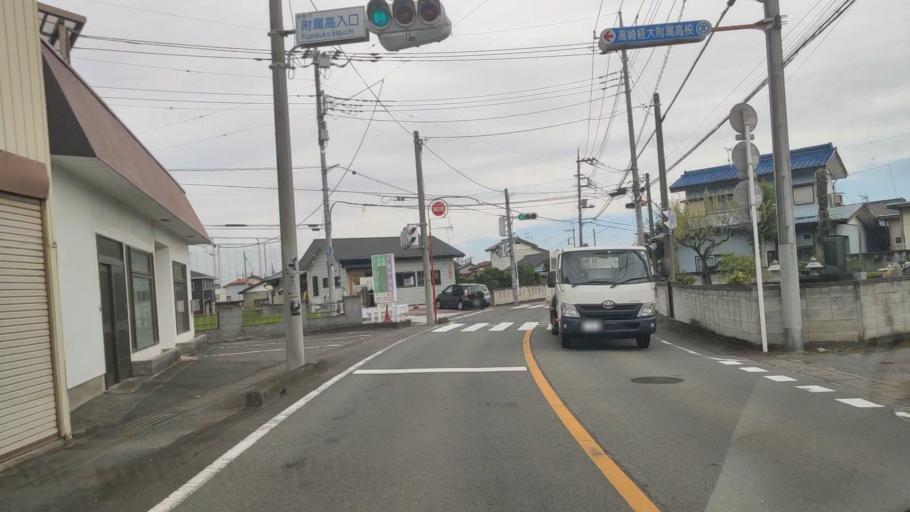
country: JP
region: Gunma
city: Takasaki
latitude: 36.3593
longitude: 138.9897
